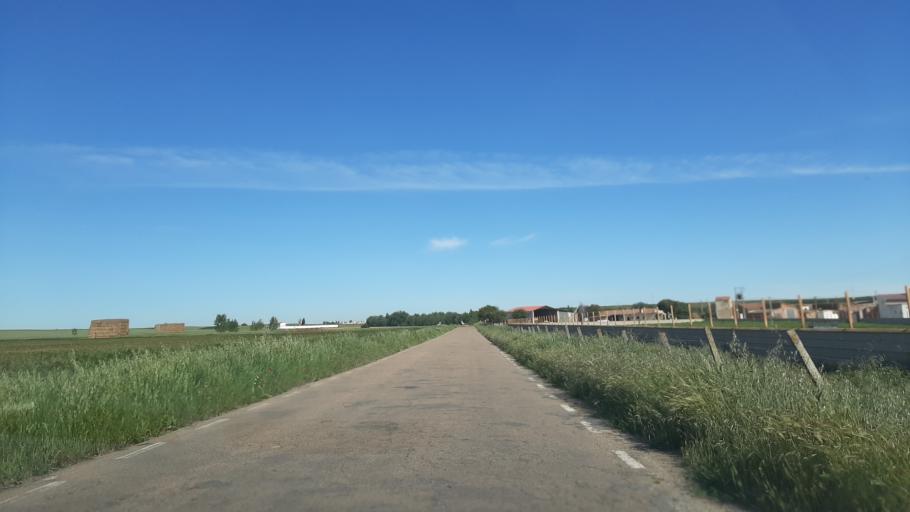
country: ES
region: Castille and Leon
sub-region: Provincia de Salamanca
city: Pedrosillo de Alba
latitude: 40.8211
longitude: -5.3967
